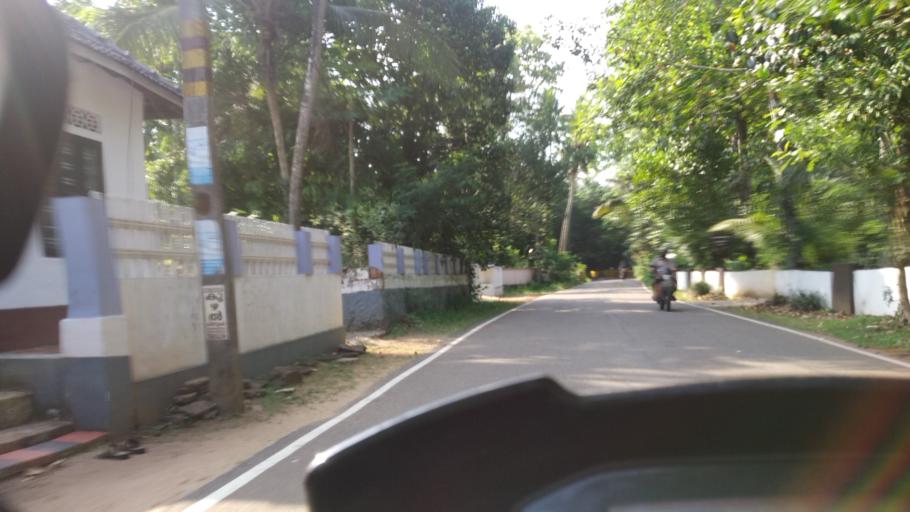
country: IN
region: Kerala
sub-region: Ernakulam
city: Piravam
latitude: 9.8628
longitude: 76.5149
